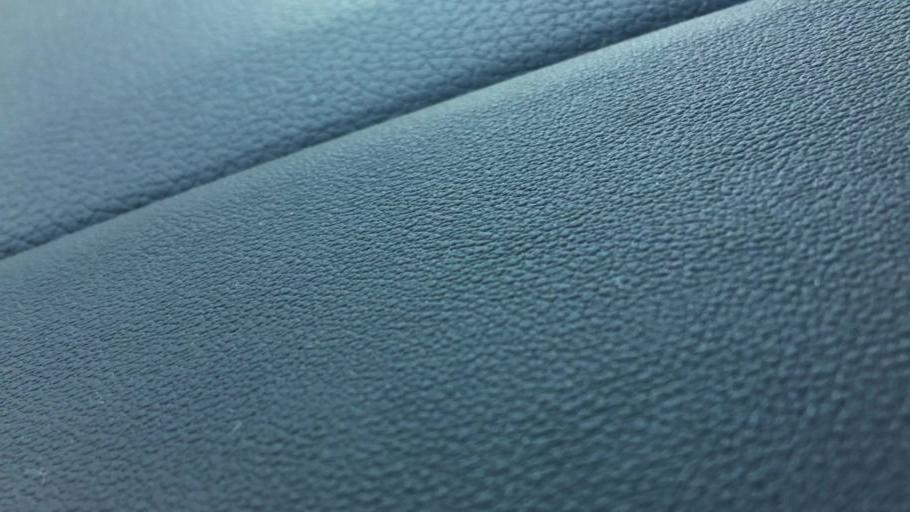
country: US
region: Virginia
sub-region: Prince William County
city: Buckhall
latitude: 38.7585
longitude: -77.4375
